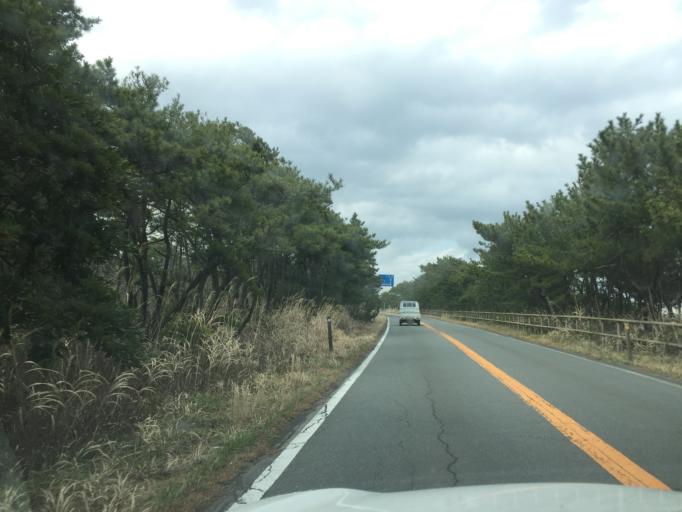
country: JP
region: Fukushima
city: Iwaki
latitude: 37.0296
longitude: 140.9712
